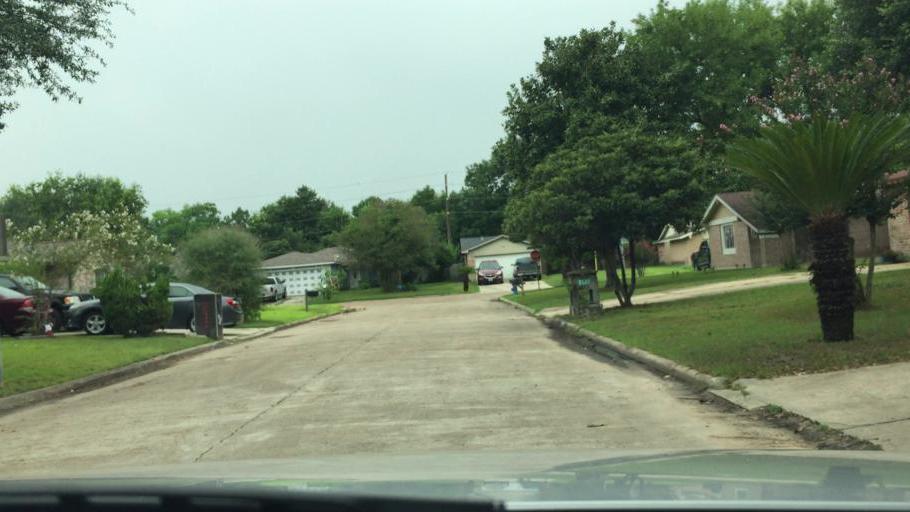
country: US
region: Texas
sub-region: Harris County
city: Hudson
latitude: 29.9066
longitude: -95.5139
